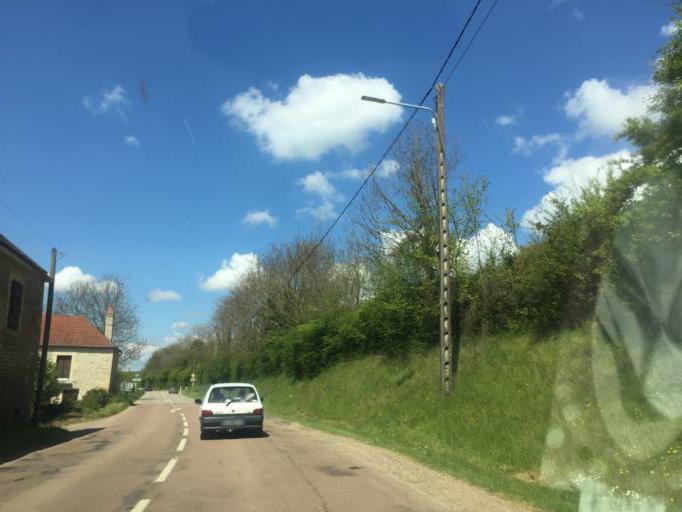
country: FR
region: Bourgogne
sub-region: Departement de la Nievre
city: Clamecy
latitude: 47.4556
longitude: 3.4680
